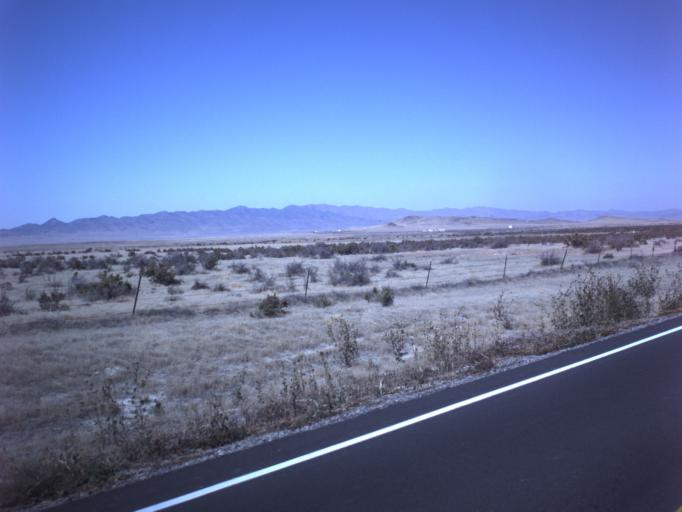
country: US
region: Utah
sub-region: Tooele County
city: Grantsville
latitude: 40.3427
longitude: -112.7449
